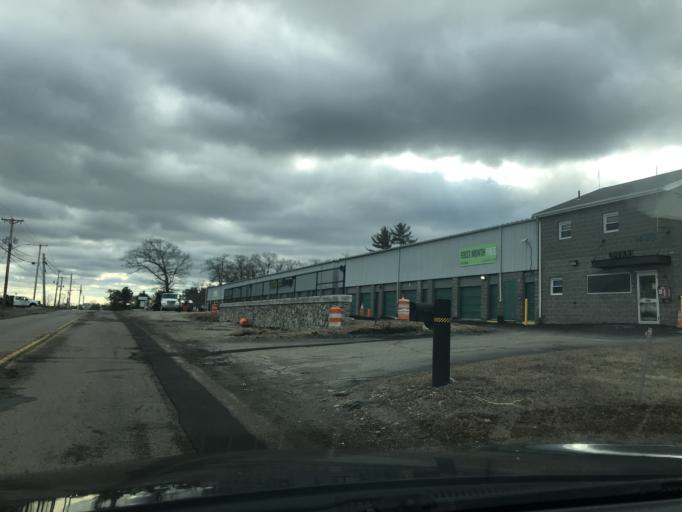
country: US
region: Massachusetts
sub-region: Plymouth County
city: Abington
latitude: 42.1432
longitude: -70.9534
